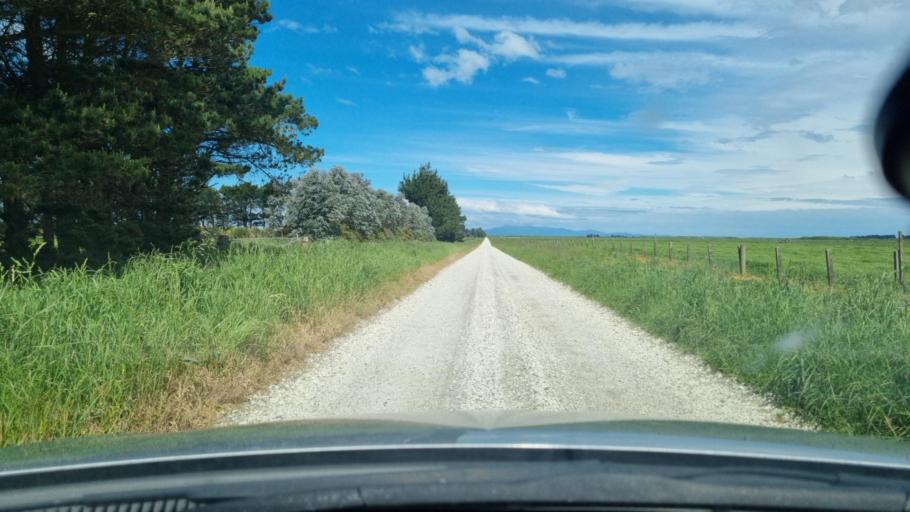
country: NZ
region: Southland
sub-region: Invercargill City
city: Invercargill
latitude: -46.3737
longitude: 168.2759
